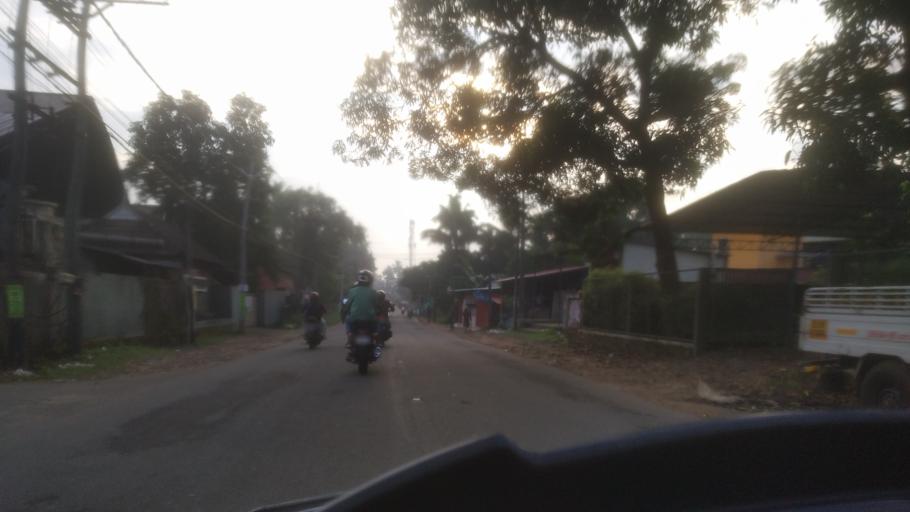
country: IN
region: Kerala
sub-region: Ernakulam
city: Perumpavur
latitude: 10.1170
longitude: 76.4442
